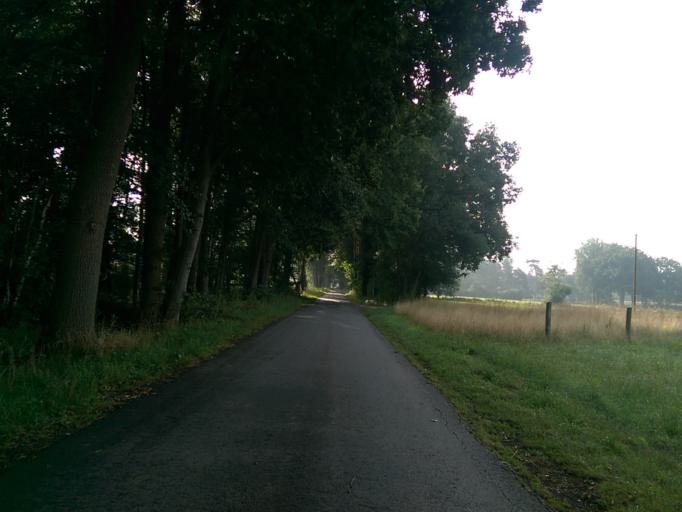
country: DE
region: North Rhine-Westphalia
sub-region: Regierungsbezirk Detmold
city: Guetersloh
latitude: 51.9175
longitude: 8.3356
